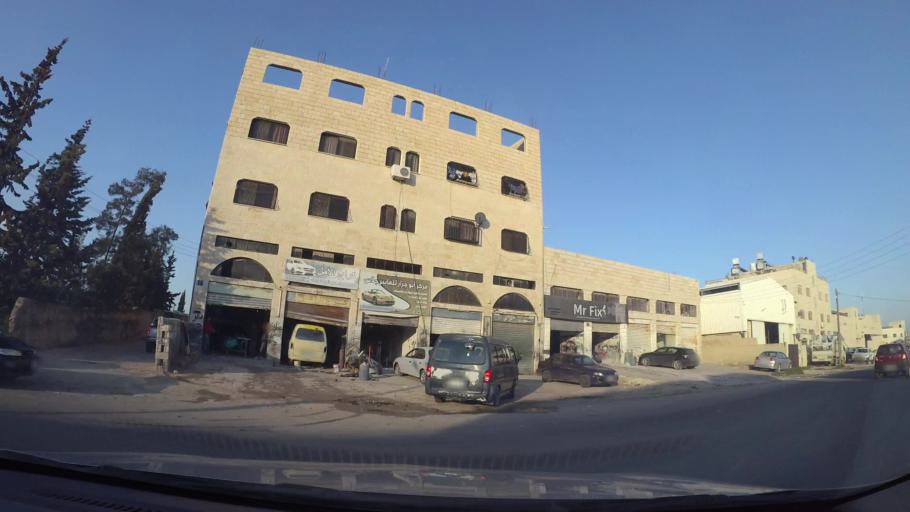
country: JO
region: Amman
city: Al Bunayyat ash Shamaliyah
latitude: 31.9089
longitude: 35.9163
